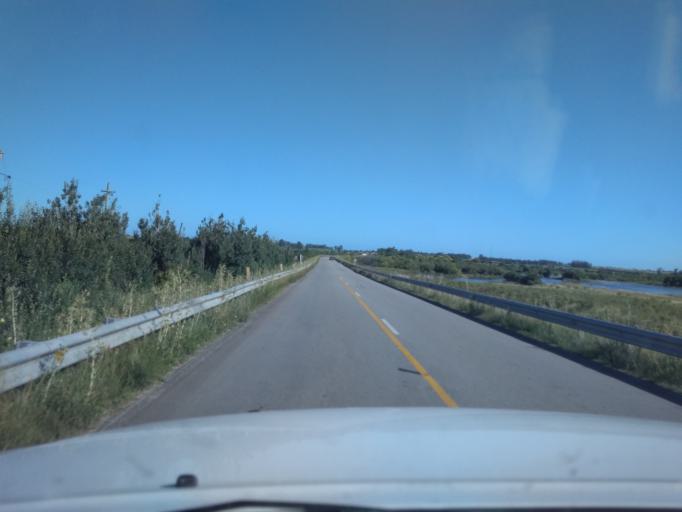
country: UY
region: Canelones
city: San Ramon
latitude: -34.3308
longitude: -55.9604
